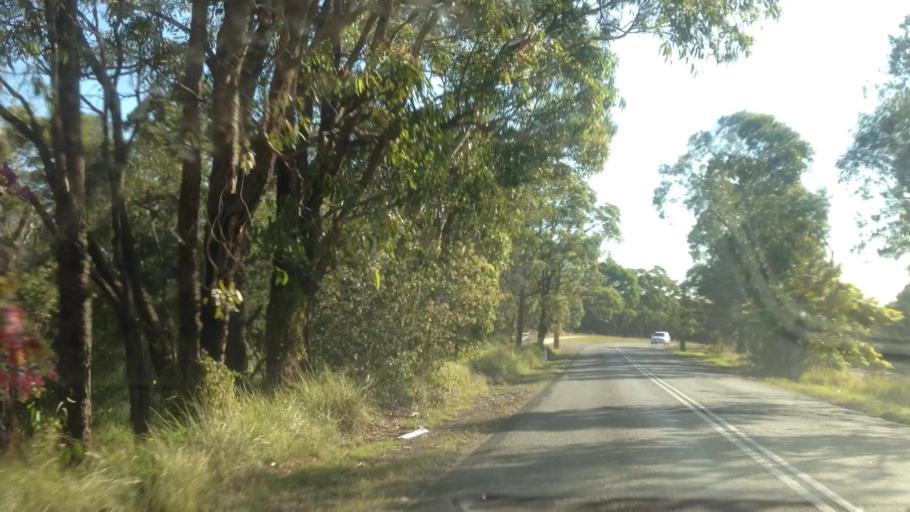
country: AU
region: New South Wales
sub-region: Lake Macquarie Shire
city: Dora Creek
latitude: -33.1080
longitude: 151.5401
